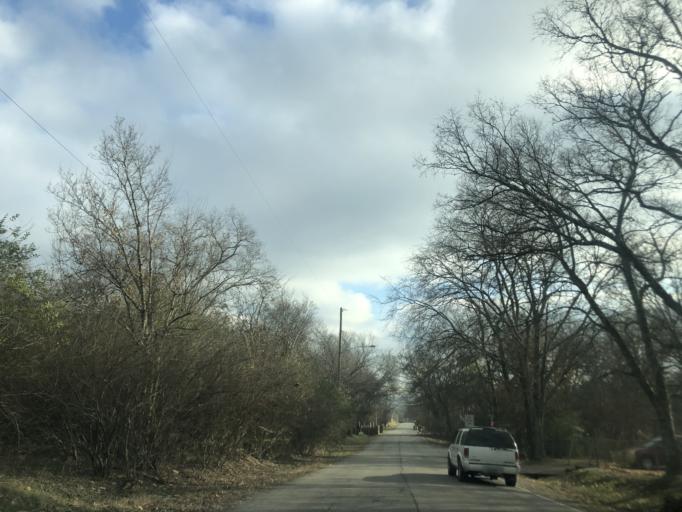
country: US
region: Tennessee
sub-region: Davidson County
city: Nashville
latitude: 36.2065
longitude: -86.7880
